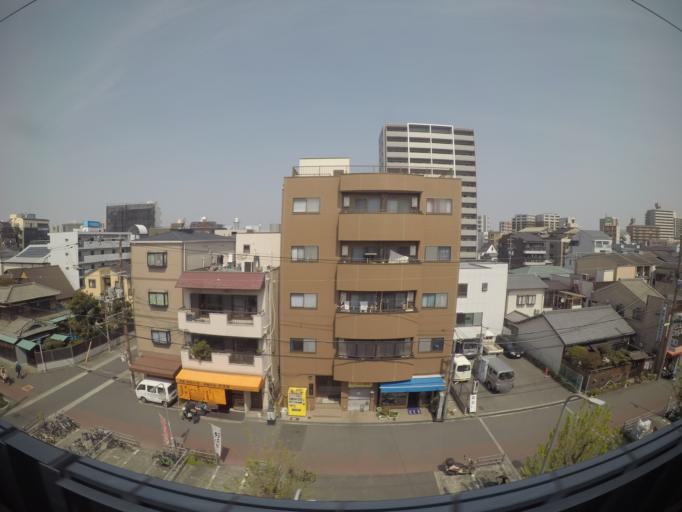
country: JP
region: Osaka
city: Suita
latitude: 34.7478
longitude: 135.5353
